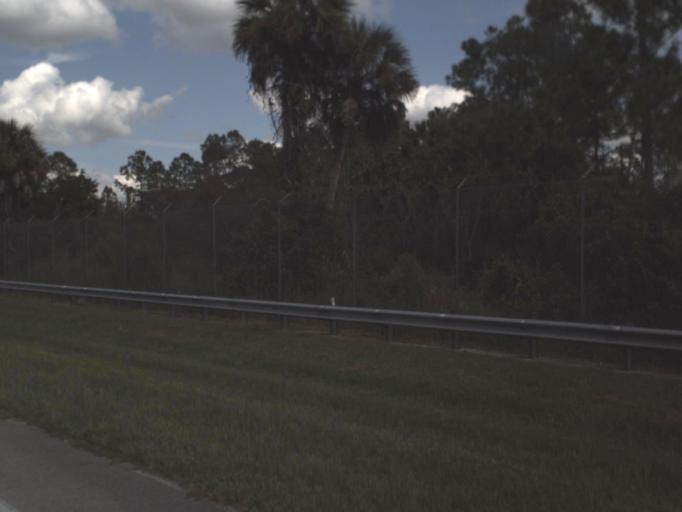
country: US
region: Florida
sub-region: Collier County
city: Immokalee
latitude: 26.1844
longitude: -81.3457
